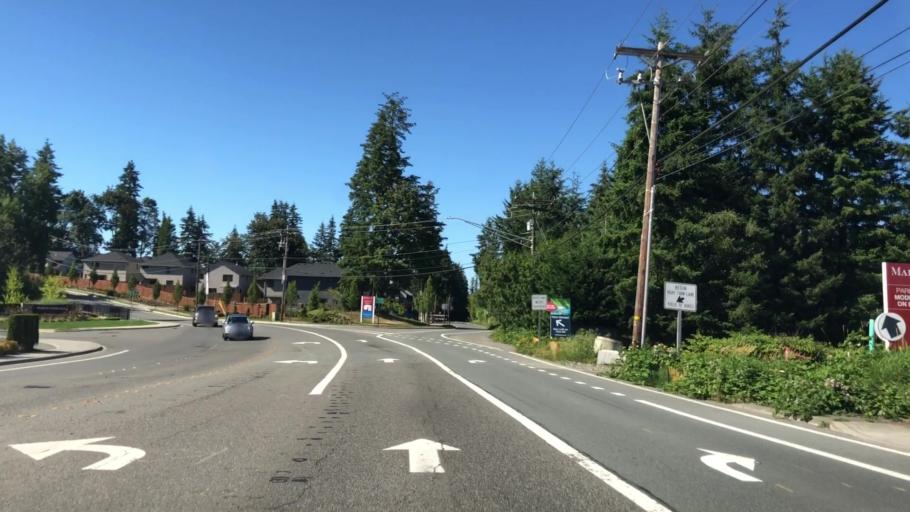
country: US
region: Washington
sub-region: Snohomish County
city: North Creek
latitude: 47.8140
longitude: -122.1822
